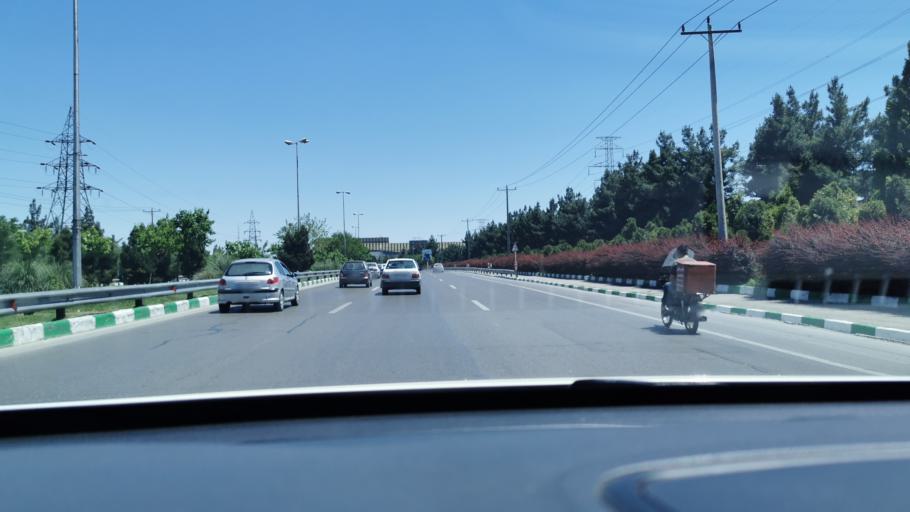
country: IR
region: Razavi Khorasan
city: Mashhad
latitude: 36.2596
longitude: 59.5866
